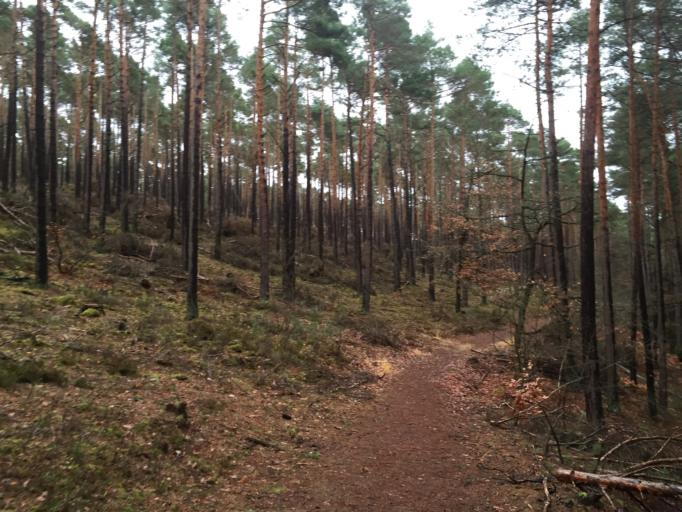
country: DE
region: Rheinland-Pfalz
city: Altleiningen
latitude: 49.5059
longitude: 8.0819
